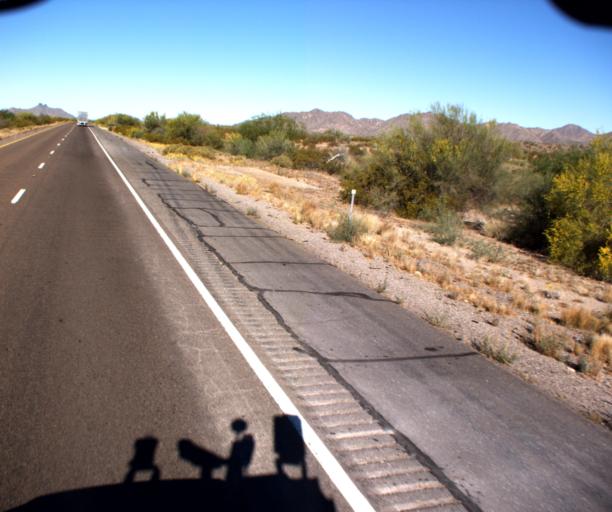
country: US
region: Arizona
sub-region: Pinal County
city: Maricopa
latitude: 32.8502
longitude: -112.3452
